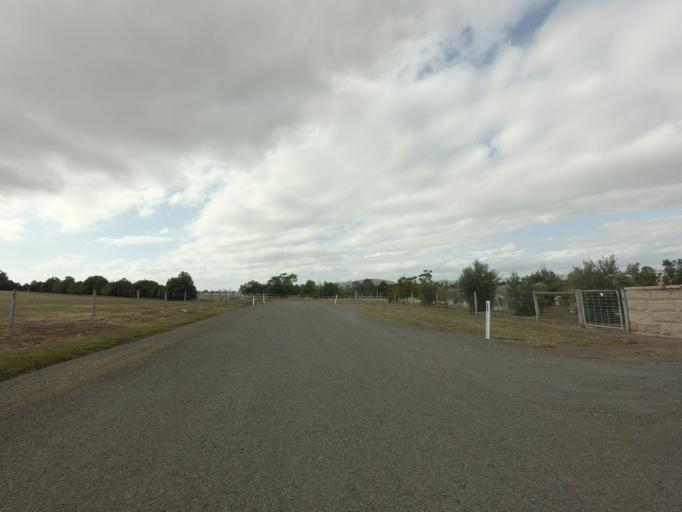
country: AU
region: Tasmania
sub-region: Clarence
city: Cambridge
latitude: -42.8383
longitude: 147.4693
